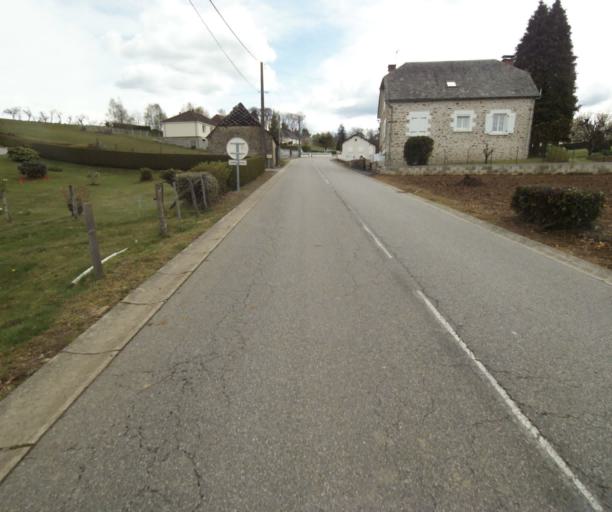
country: FR
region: Limousin
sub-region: Departement de la Correze
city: Laguenne
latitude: 45.2112
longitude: 1.8666
